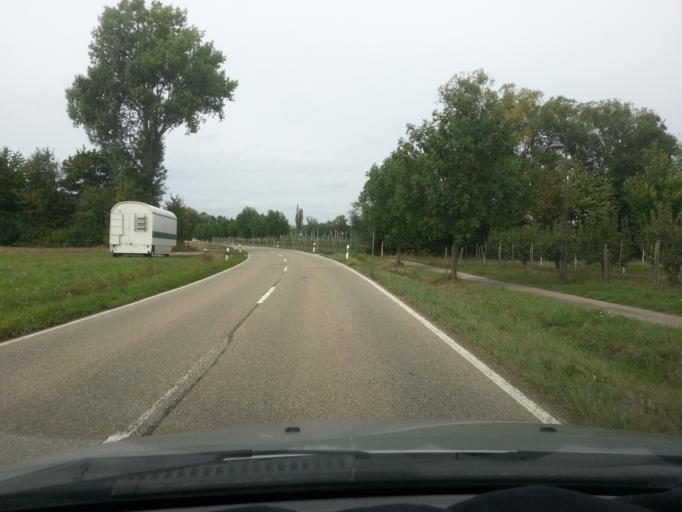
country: DE
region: Rheinland-Pfalz
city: Grossfischlingen
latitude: 49.2717
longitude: 8.1756
